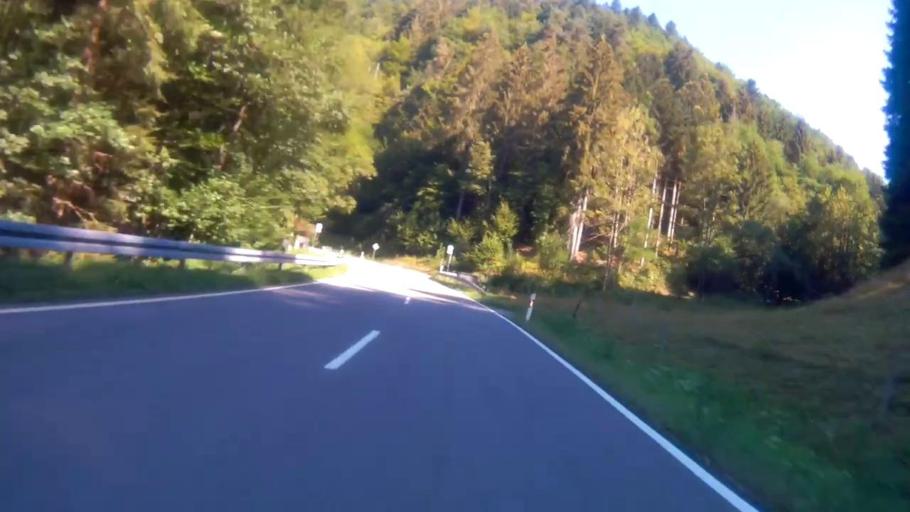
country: DE
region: Baden-Wuerttemberg
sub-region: Freiburg Region
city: Zell im Wiesental
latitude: 47.7358
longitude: 7.7696
